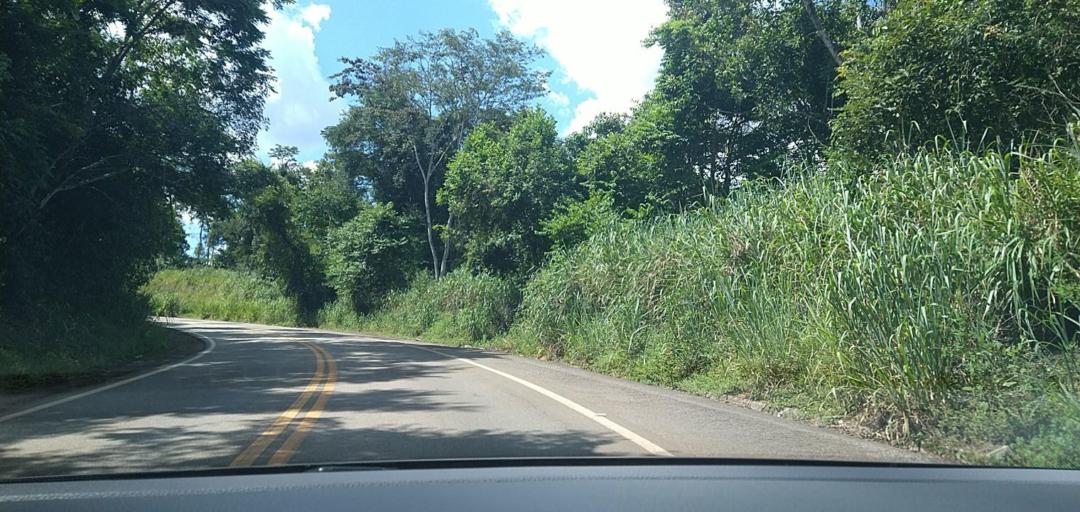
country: BR
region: Minas Gerais
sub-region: Joao Monlevade
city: Joao Monlevade
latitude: -19.8671
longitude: -43.1202
